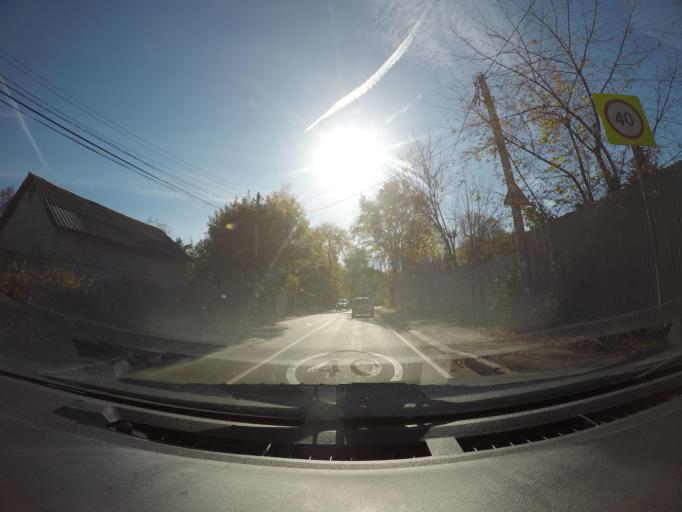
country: RU
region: Moskovskaya
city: Rodniki
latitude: 55.6417
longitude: 38.0531
